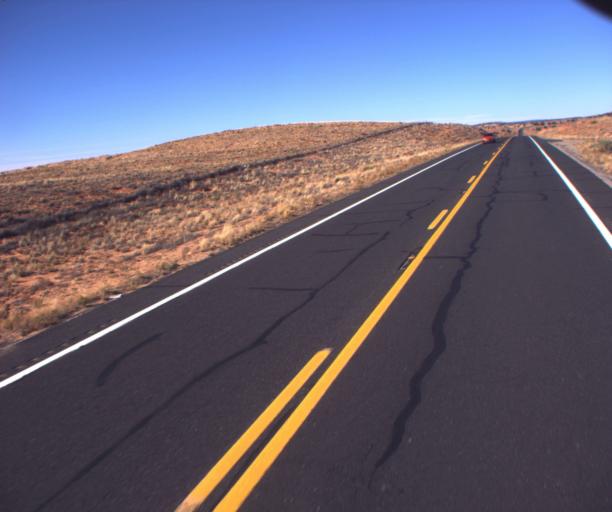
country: US
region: Arizona
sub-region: Coconino County
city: Kaibito
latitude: 36.4905
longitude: -110.7054
